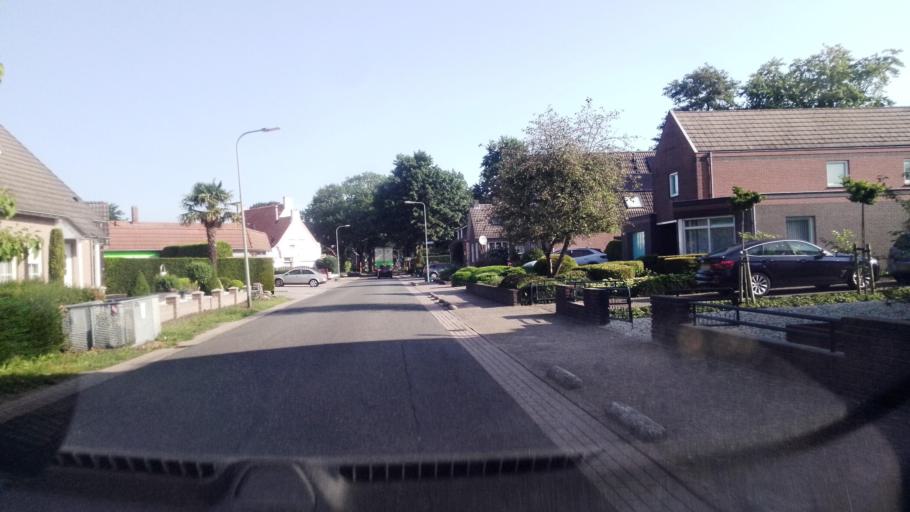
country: NL
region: Limburg
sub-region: Gemeente Bergen
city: Wellerlooi
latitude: 51.4599
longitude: 6.0845
